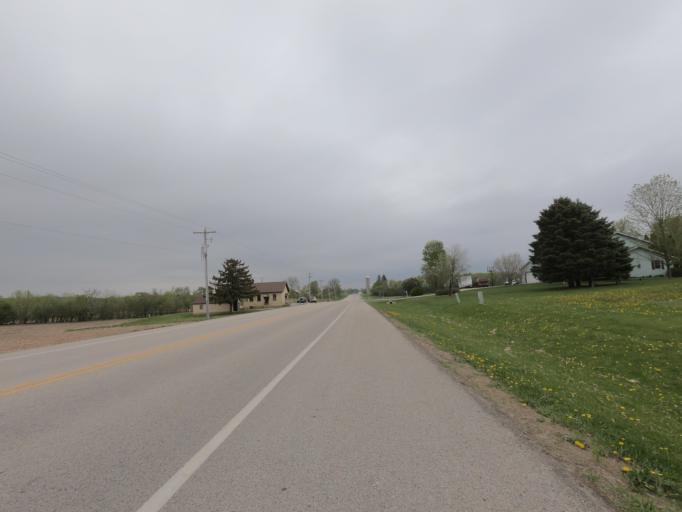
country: US
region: Wisconsin
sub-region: Jefferson County
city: Johnson Creek
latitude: 43.0346
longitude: -88.7734
